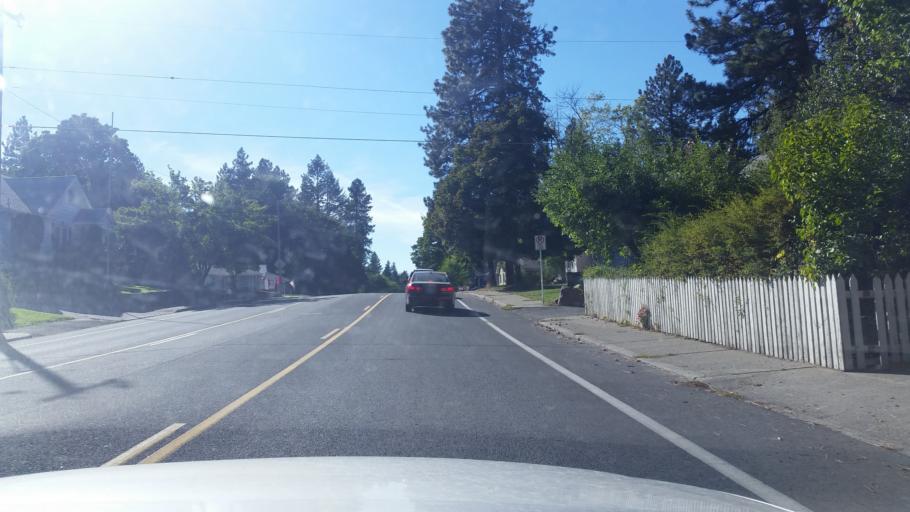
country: US
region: Washington
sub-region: Spokane County
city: Spokane
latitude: 47.6282
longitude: -117.4081
